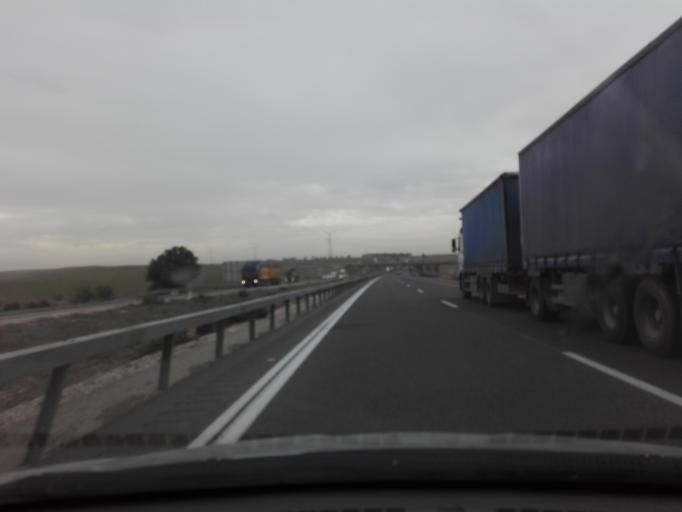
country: IL
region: Southern District
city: Qiryat Gat
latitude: 31.5302
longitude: 34.7918
